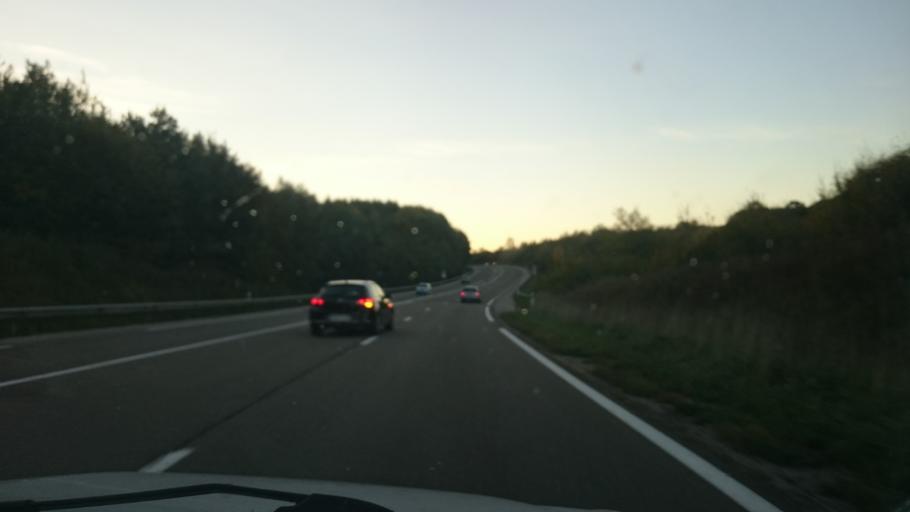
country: FR
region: Franche-Comte
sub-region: Departement du Jura
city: Poligny
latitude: 46.8381
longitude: 5.6774
